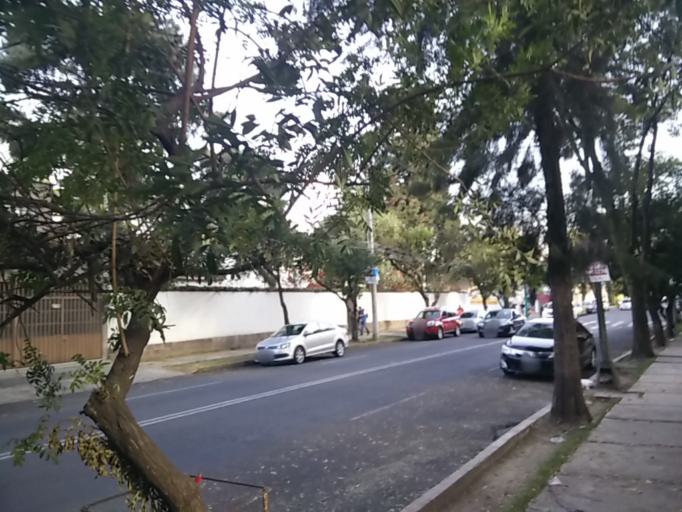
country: MX
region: Mexico
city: Colonia Lindavista
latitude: 19.4940
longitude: -99.1273
